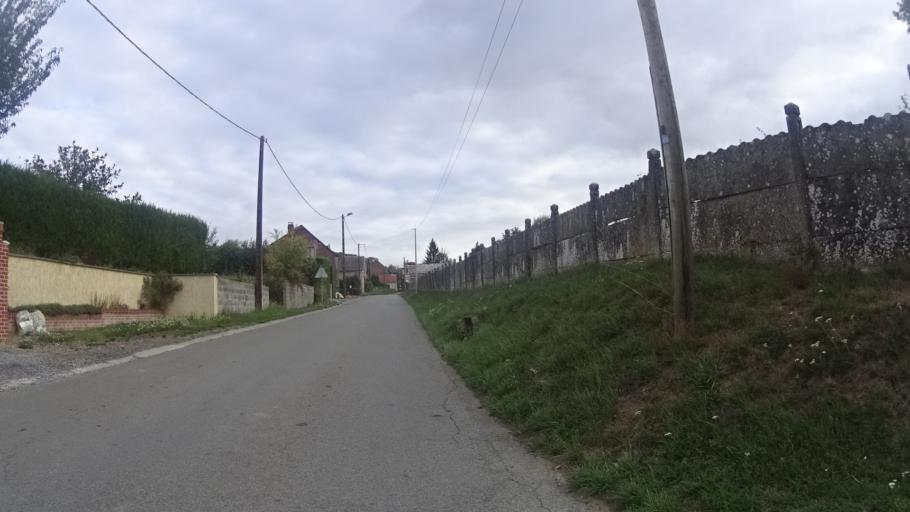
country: FR
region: Picardie
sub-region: Departement de l'Aisne
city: Guise
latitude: 49.9349
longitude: 3.5824
